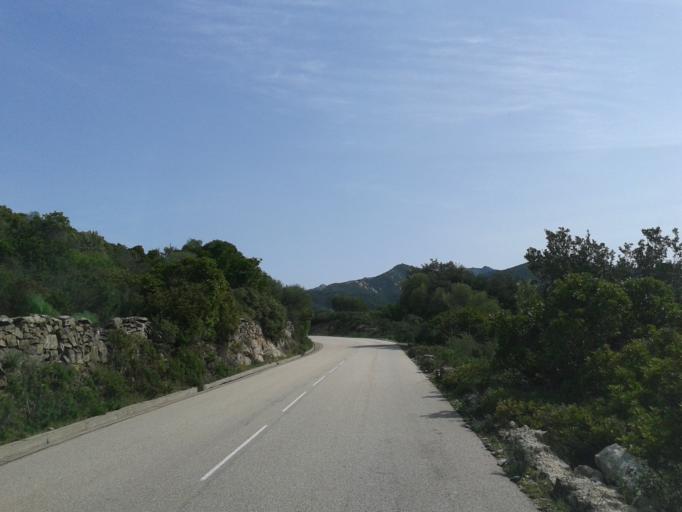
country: FR
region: Corsica
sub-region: Departement de la Haute-Corse
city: Monticello
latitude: 42.6529
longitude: 9.1066
